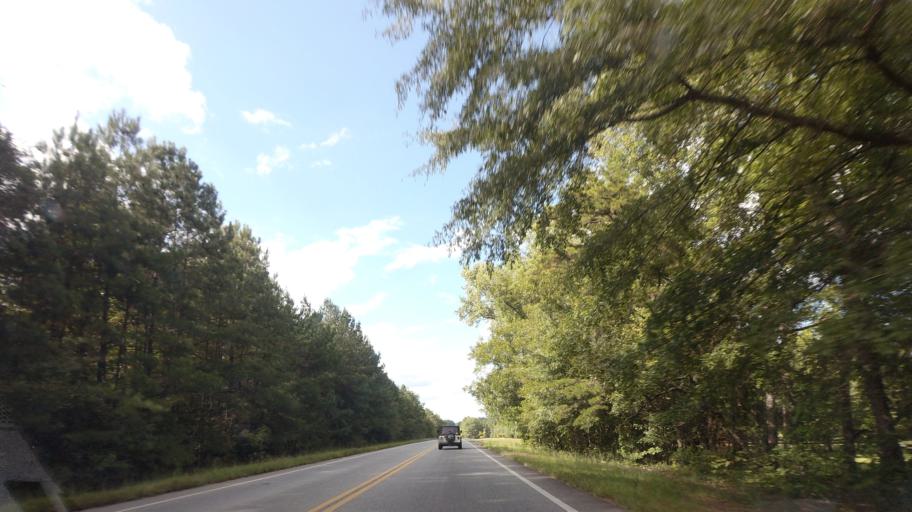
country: US
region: Georgia
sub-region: Bibb County
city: Macon
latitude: 32.9702
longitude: -83.7278
